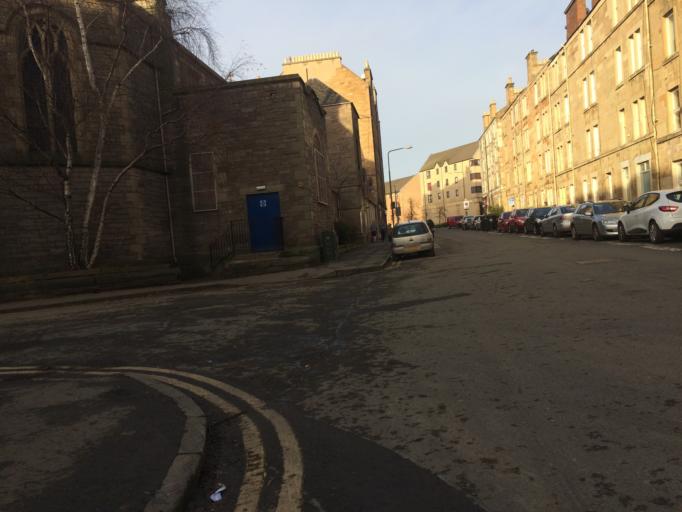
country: GB
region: Scotland
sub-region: Edinburgh
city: Edinburgh
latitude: 55.9423
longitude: -3.2199
